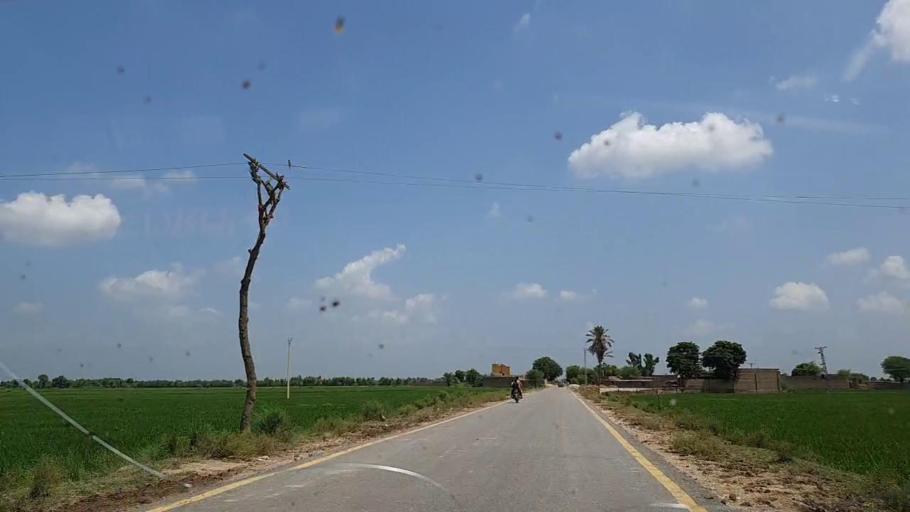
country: PK
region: Sindh
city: Tharu Shah
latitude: 26.9803
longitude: 68.0831
